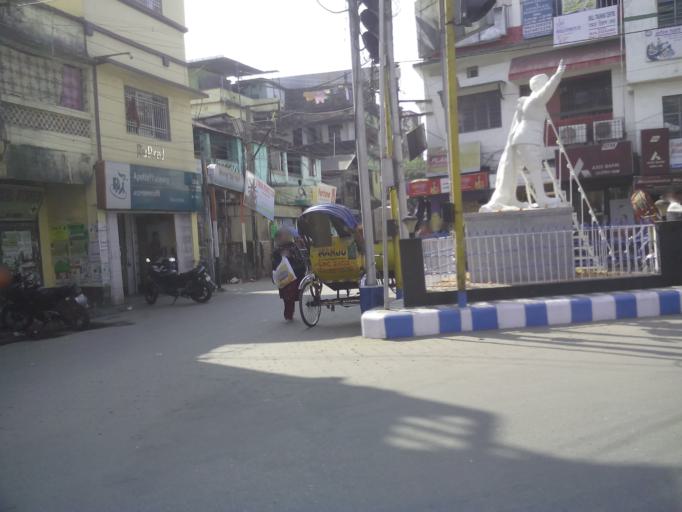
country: IN
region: West Bengal
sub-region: Darjiling
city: Shiliguri
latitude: 26.7080
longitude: 88.4344
